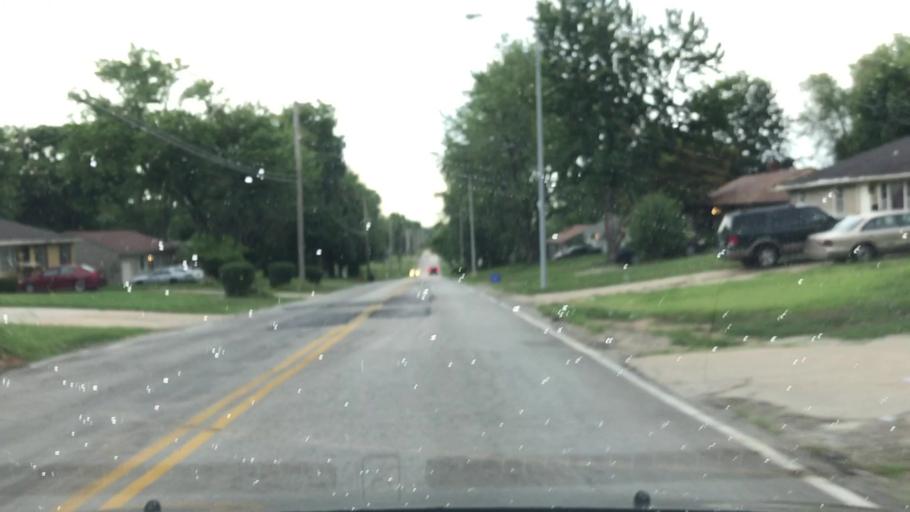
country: US
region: Missouri
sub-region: Jackson County
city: Grandview
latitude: 38.9302
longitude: -94.4984
